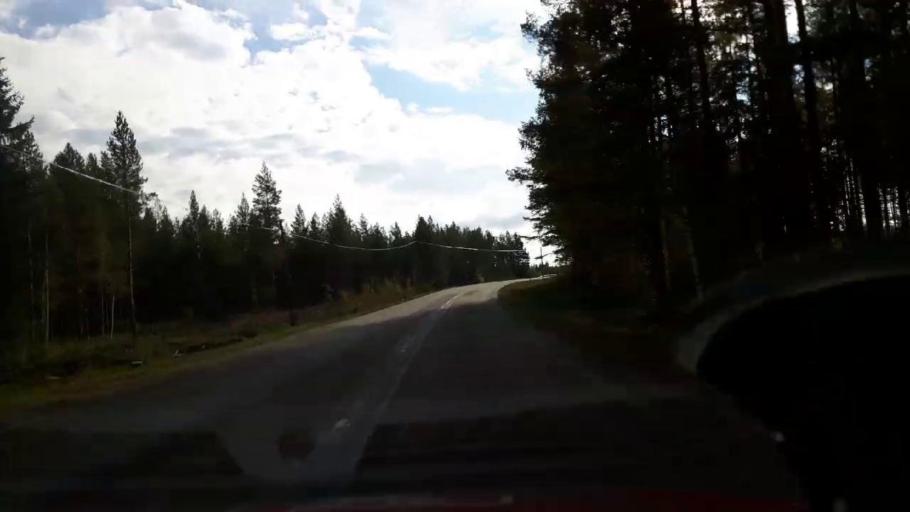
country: SE
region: Jaemtland
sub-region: Harjedalens Kommun
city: Sveg
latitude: 62.1252
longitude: 15.0302
